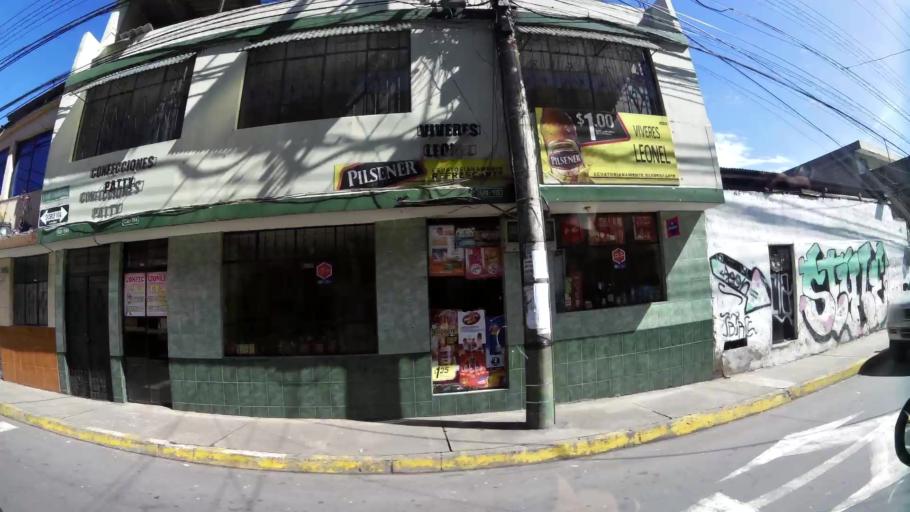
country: EC
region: Pichincha
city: Quito
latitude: -0.2787
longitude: -78.5556
